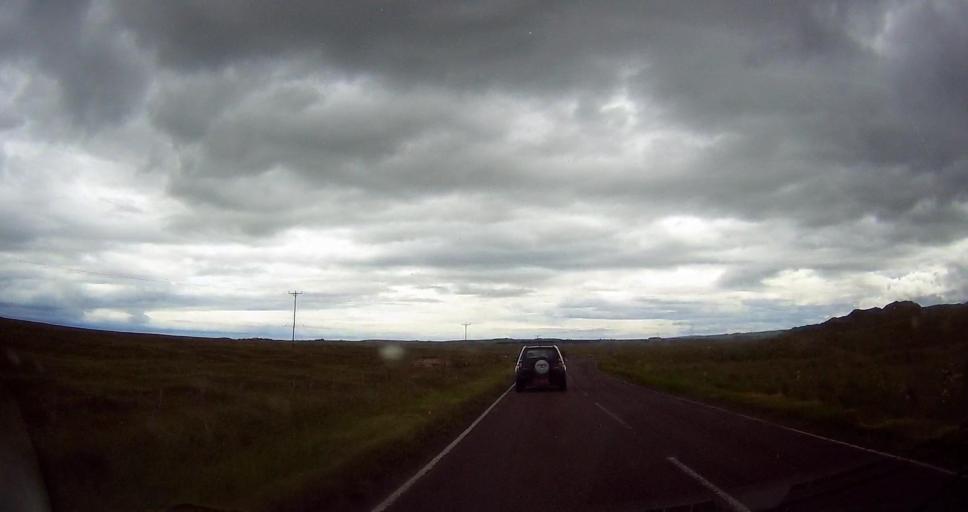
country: GB
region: Scotland
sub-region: Highland
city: Thurso
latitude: 58.6092
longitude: -3.3436
